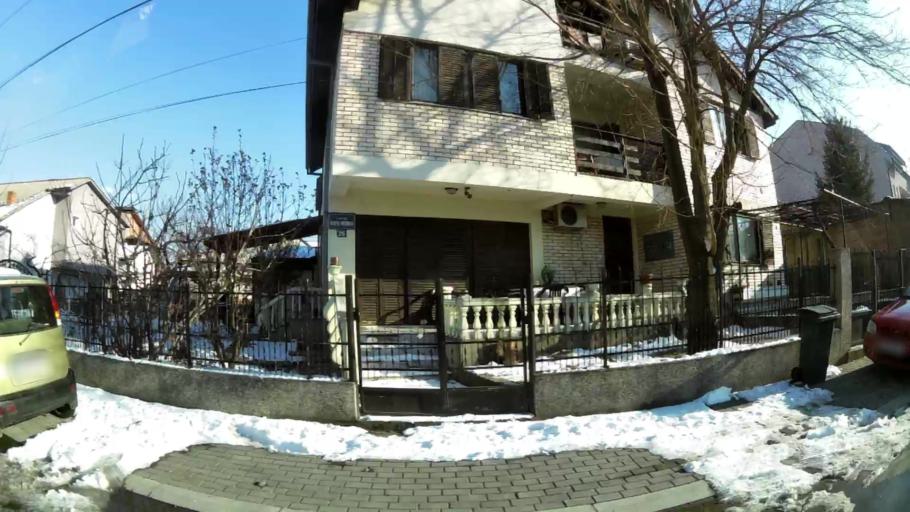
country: MK
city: Krushopek
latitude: 42.0014
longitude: 21.3795
